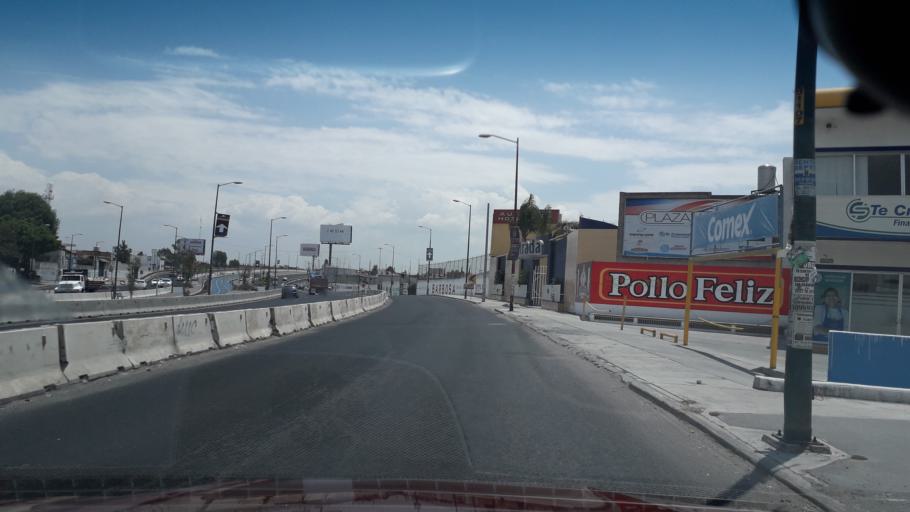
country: MX
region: Puebla
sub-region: Puebla
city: El Capulo (La Quebradora)
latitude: 18.9925
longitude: -98.2495
